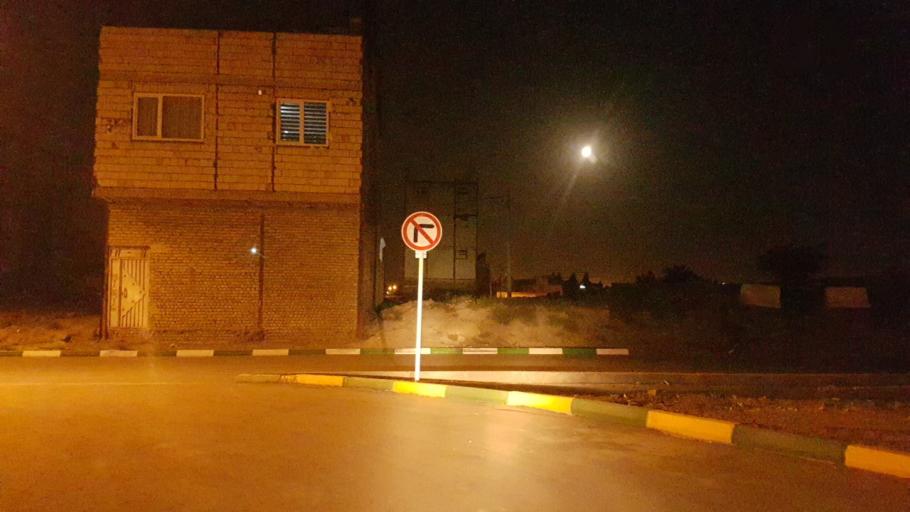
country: IR
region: Razavi Khorasan
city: Mashhad
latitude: 36.3574
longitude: 59.5642
